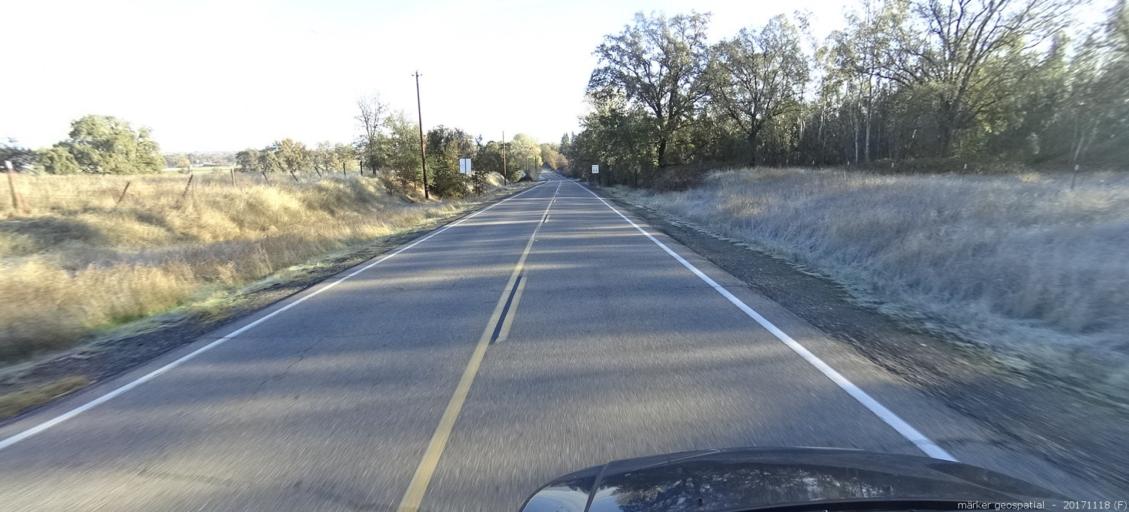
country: US
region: California
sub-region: Shasta County
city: Anderson
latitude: 40.4392
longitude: -122.2688
